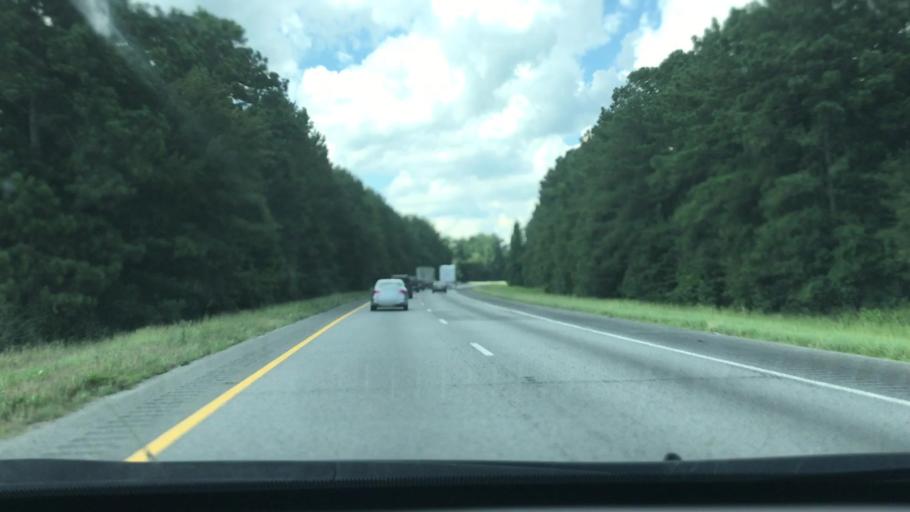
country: US
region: South Carolina
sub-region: Clarendon County
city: Manning
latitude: 33.6626
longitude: -80.2764
